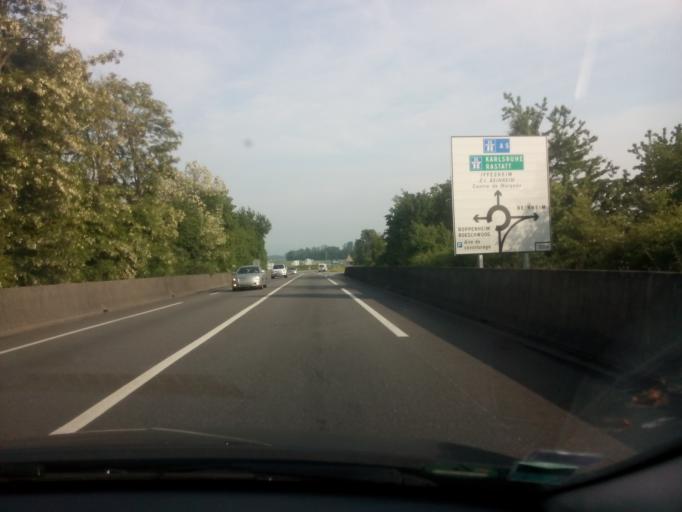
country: FR
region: Alsace
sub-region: Departement du Bas-Rhin
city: Roppenheim
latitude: 48.8496
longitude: 8.0621
